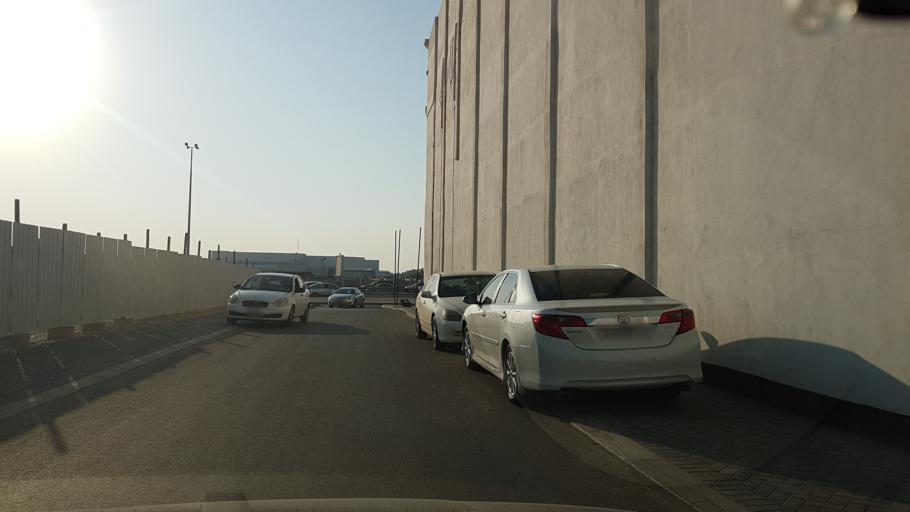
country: BH
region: Northern
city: Madinat `Isa
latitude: 26.1886
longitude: 50.5369
